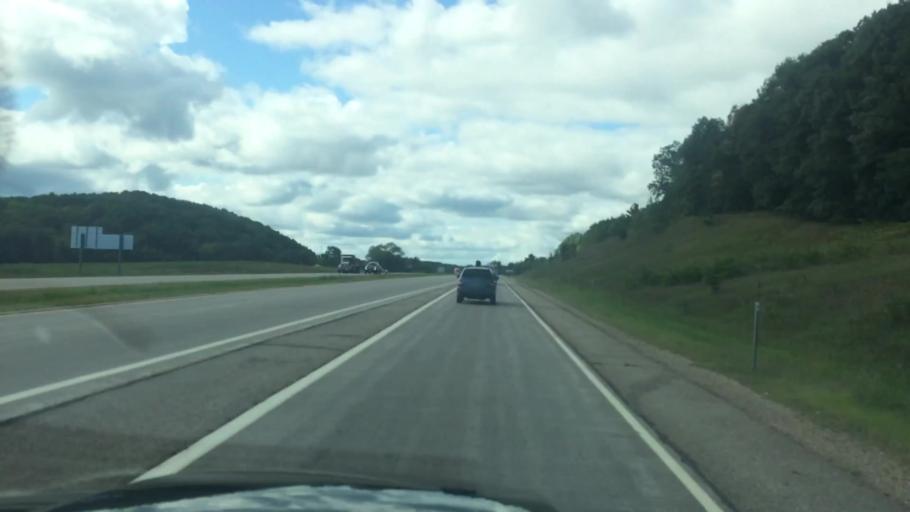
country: US
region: Wisconsin
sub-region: Waupaca County
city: Waupaca
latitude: 44.3407
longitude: -89.0718
